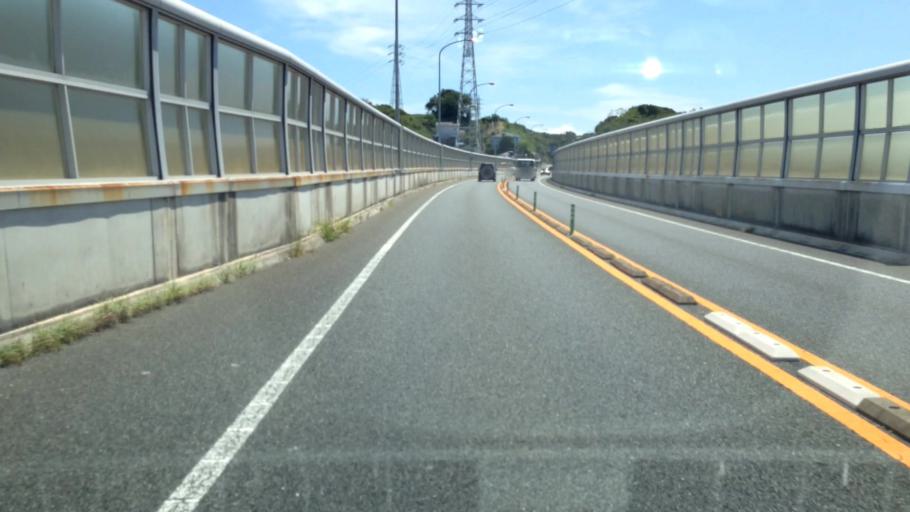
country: JP
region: Kanagawa
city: Yokosuka
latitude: 35.2183
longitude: 139.6374
